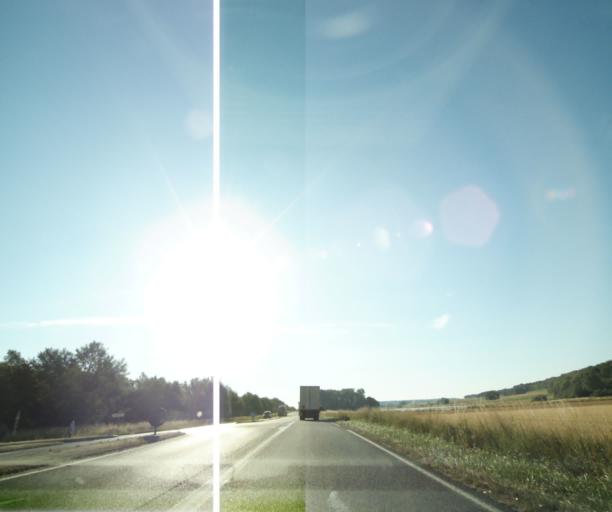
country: FR
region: Ile-de-France
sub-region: Departement de Seine-et-Marne
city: La Grande-Paroisse
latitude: 48.3612
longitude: 2.8881
